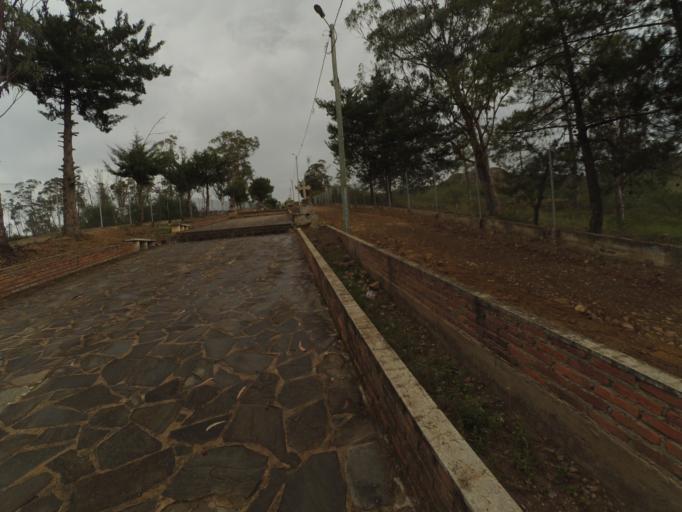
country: BO
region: Chuquisaca
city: Padilla
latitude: -19.3142
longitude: -64.3079
